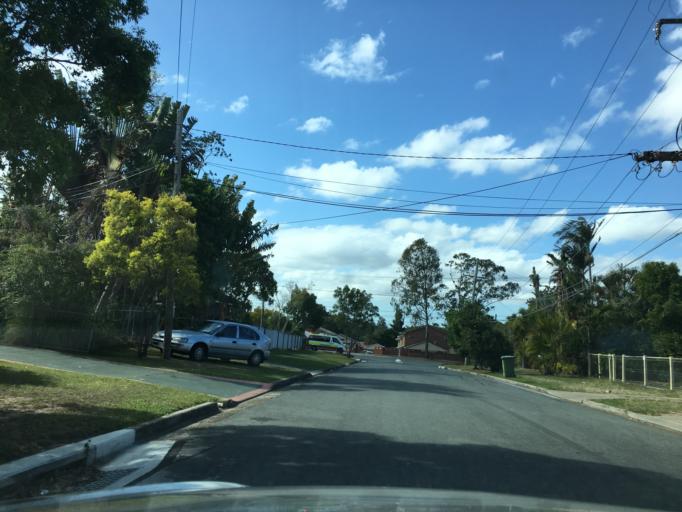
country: AU
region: Queensland
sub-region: Logan
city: Waterford West
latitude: -27.6759
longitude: 153.1272
